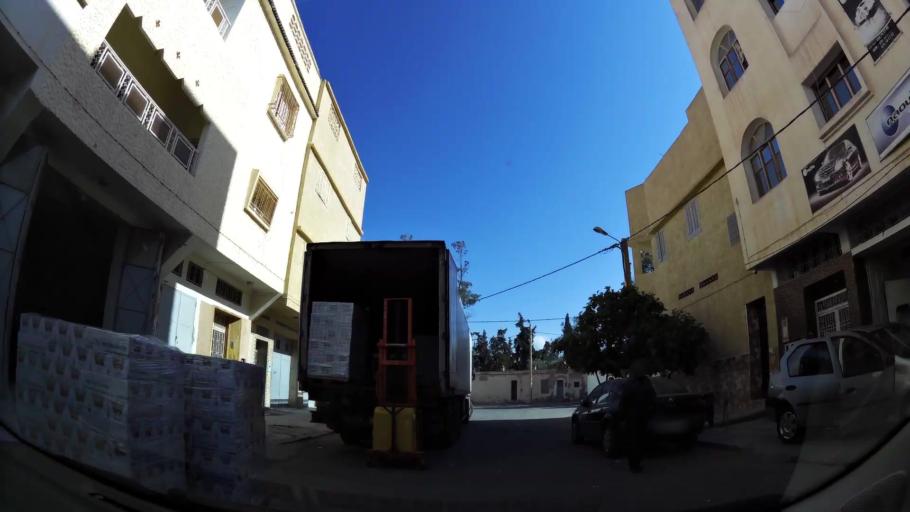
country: MA
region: Oriental
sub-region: Oujda-Angad
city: Oujda
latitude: 34.6869
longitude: -1.9219
